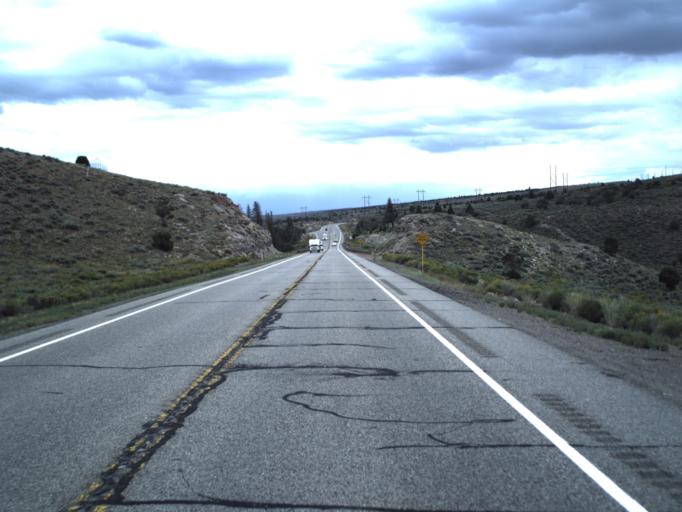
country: US
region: Utah
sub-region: Carbon County
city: Helper
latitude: 39.8277
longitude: -110.9563
